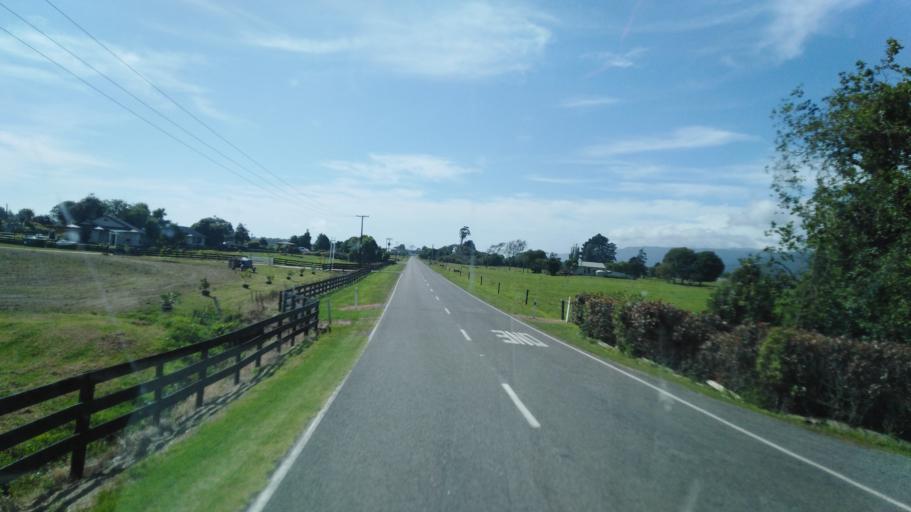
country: NZ
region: West Coast
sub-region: Buller District
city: Westport
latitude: -41.2591
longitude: 172.1322
